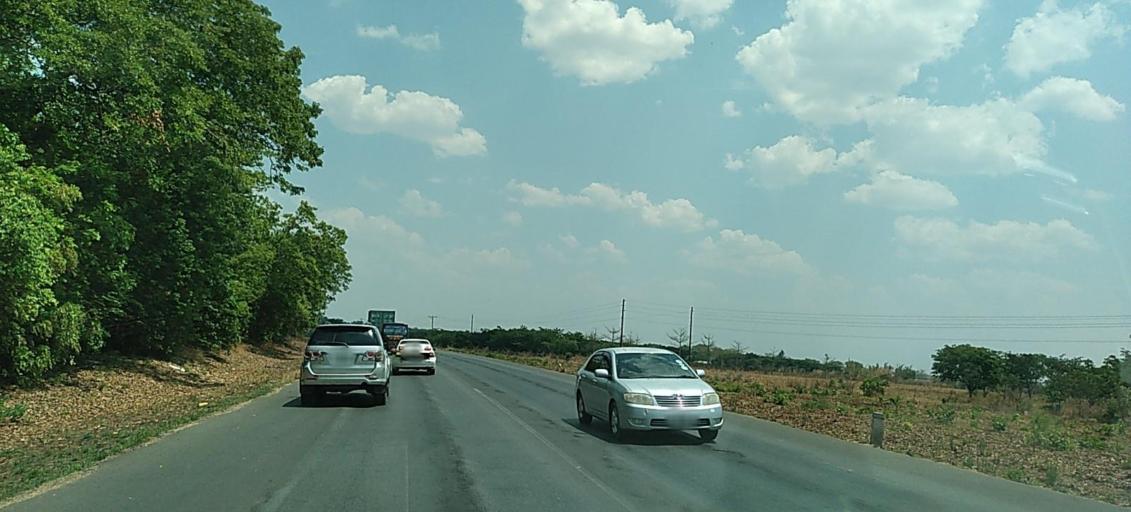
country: ZM
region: Central
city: Kabwe
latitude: -14.3094
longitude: 28.5449
